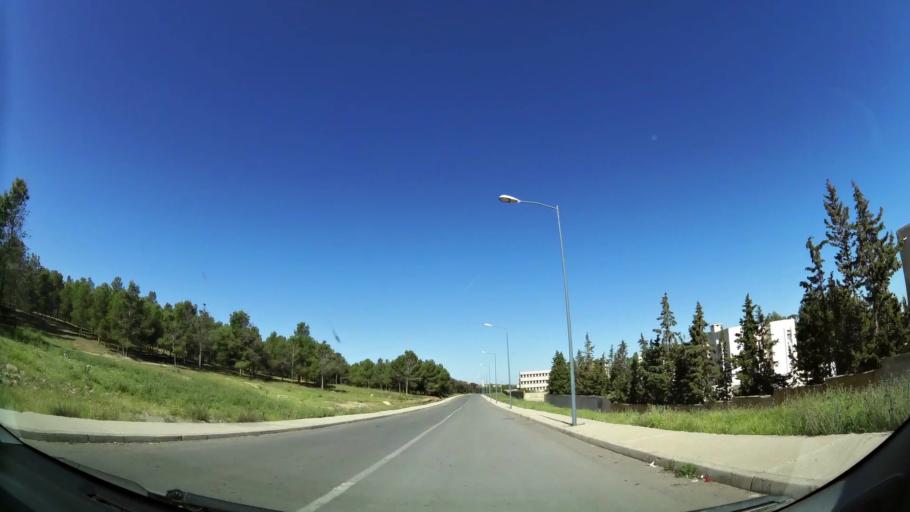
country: MA
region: Oriental
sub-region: Oujda-Angad
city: Oujda
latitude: 34.6479
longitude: -1.8951
